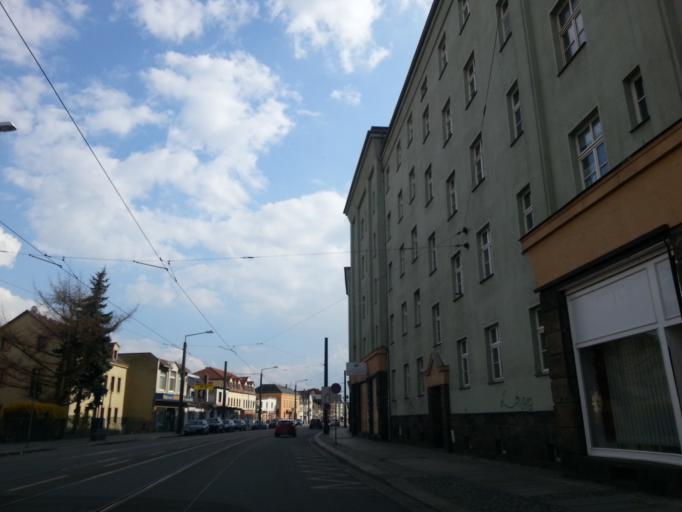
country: DE
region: Saxony
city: Dresden
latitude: 51.0823
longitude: 13.7123
